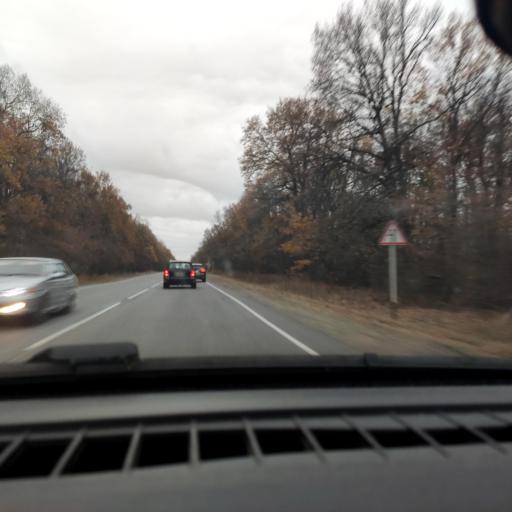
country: RU
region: Voronezj
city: Devitsa
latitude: 51.6175
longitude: 38.9843
